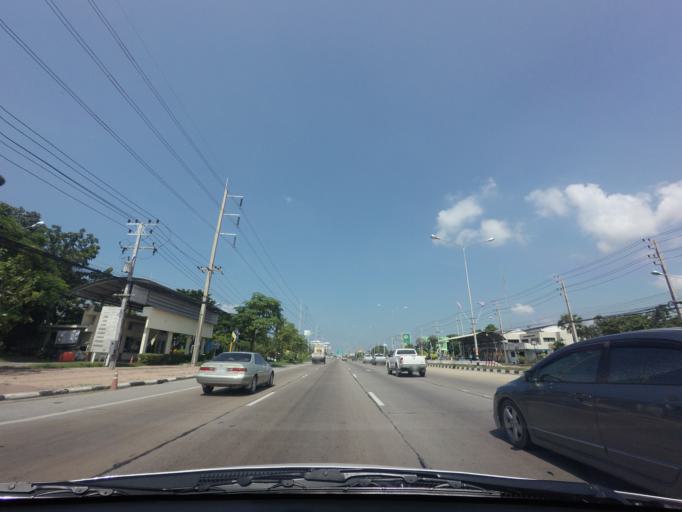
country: TH
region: Nakhon Pathom
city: Nakhon Chai Si
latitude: 13.7753
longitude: 100.1790
